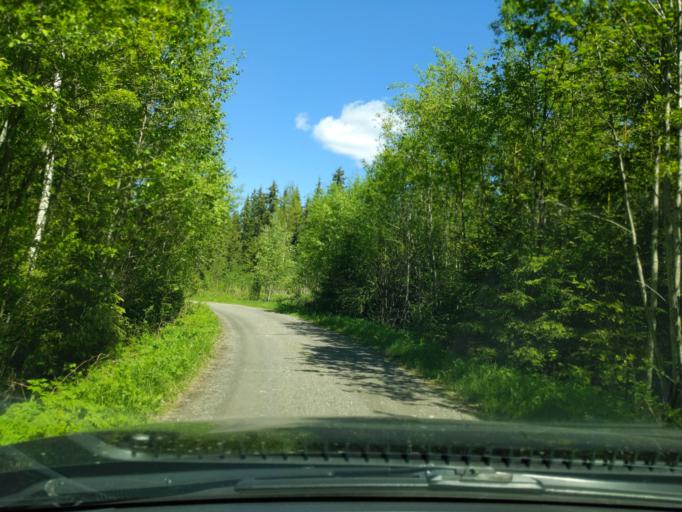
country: FI
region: Paijanne Tavastia
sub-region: Lahti
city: Lahti
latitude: 61.0586
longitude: 25.7013
